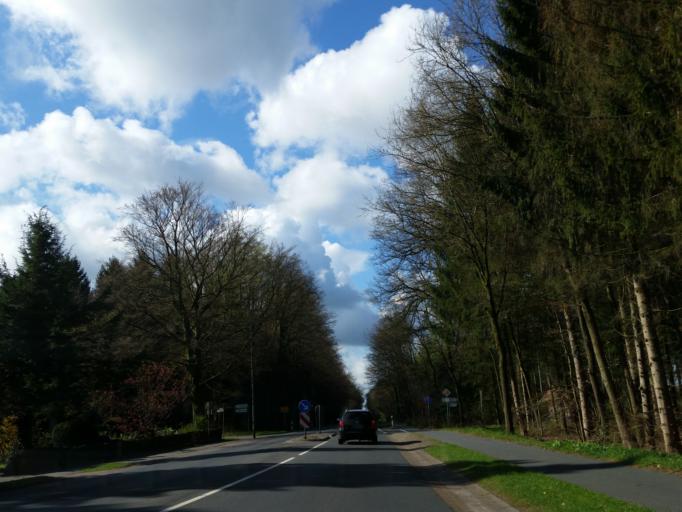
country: DE
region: Lower Saxony
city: Ahausen
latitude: 53.0754
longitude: 9.3539
